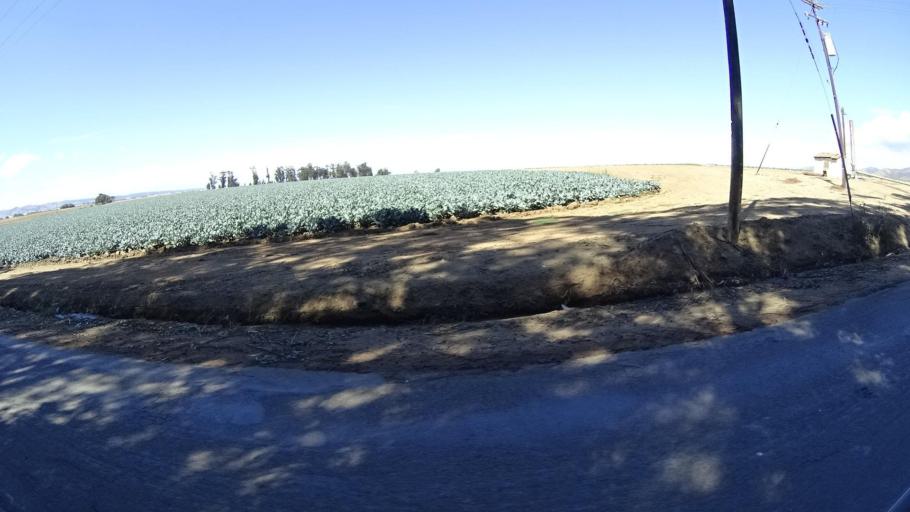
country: US
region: California
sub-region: Monterey County
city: Chualar
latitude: 36.6529
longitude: -121.5598
